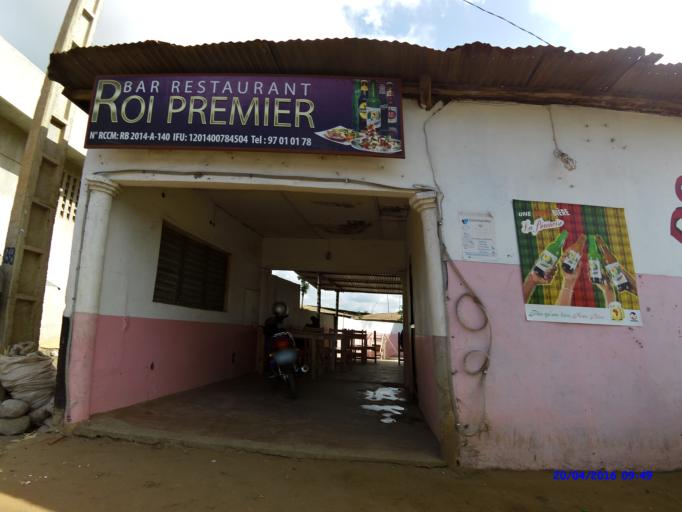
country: BJ
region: Atlantique
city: Hevie
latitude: 6.3886
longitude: 2.3022
